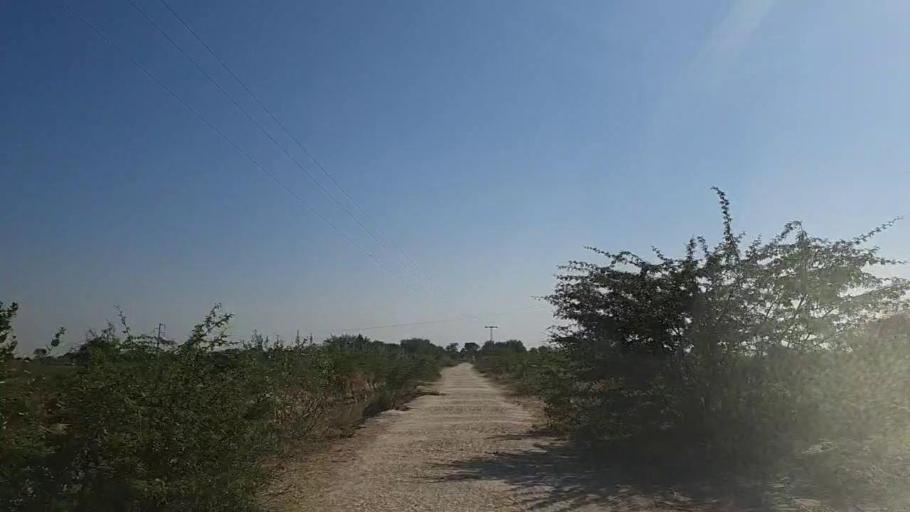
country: PK
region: Sindh
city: Samaro
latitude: 25.2334
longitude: 69.4842
